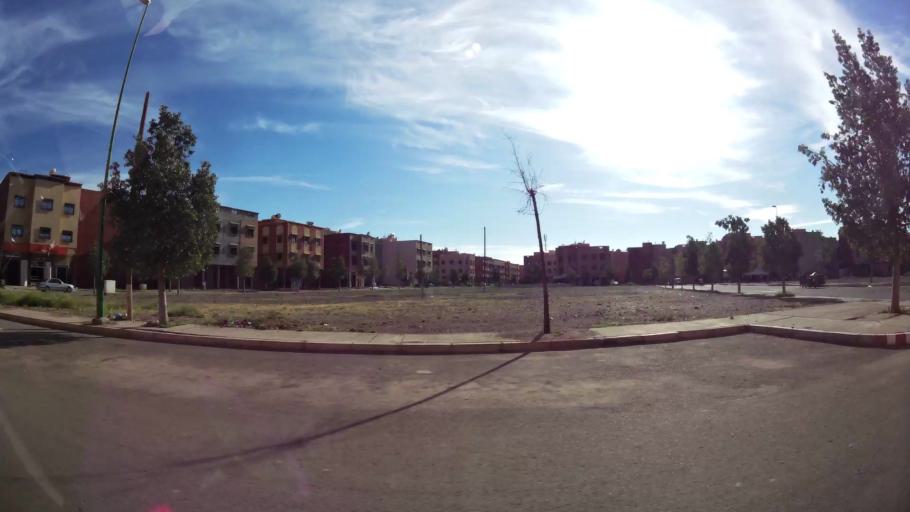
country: MA
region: Marrakech-Tensift-Al Haouz
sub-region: Marrakech
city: Marrakesh
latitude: 31.6862
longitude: -8.0716
